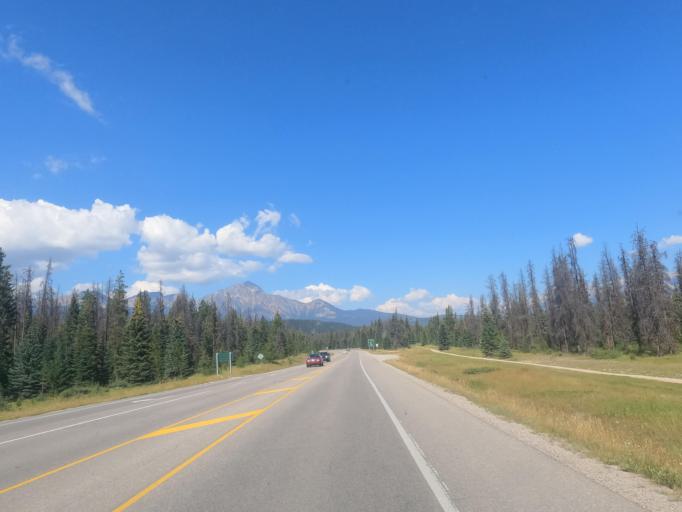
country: CA
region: Alberta
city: Jasper Park Lodge
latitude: 52.8552
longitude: -118.0780
